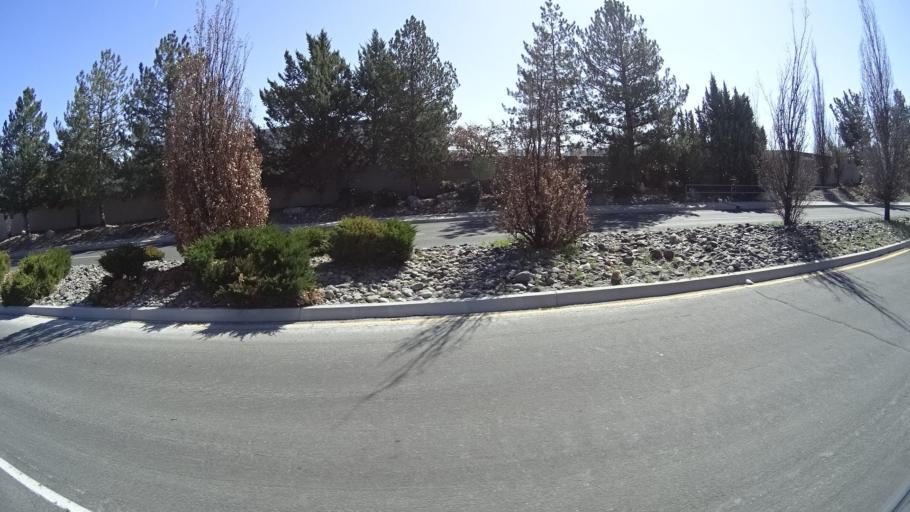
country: US
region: Nevada
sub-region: Washoe County
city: Reno
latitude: 39.4801
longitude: -119.8002
